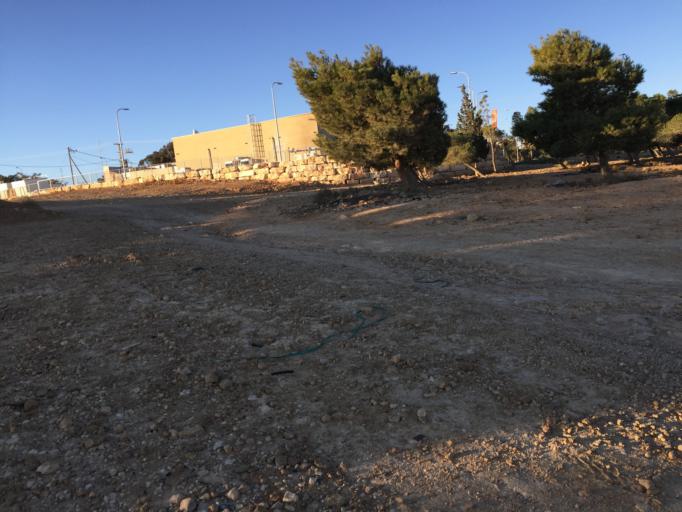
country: IL
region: Southern District
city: Mitzpe Ramon
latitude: 30.6132
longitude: 34.8053
